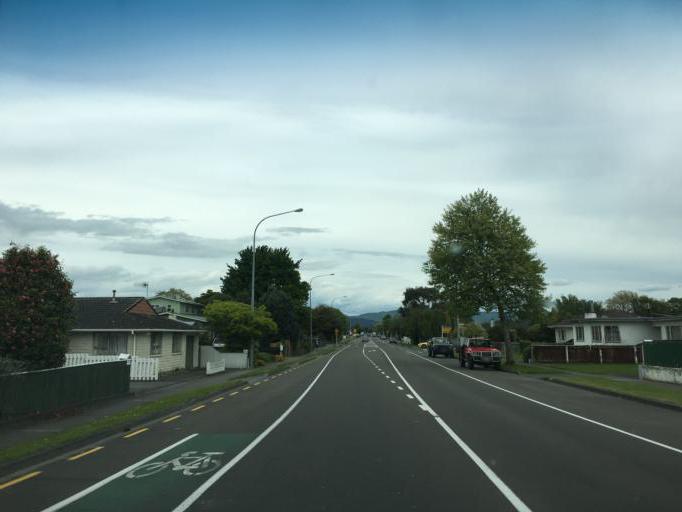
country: NZ
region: Manawatu-Wanganui
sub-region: Palmerston North City
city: Palmerston North
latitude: -40.3608
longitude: 175.5924
